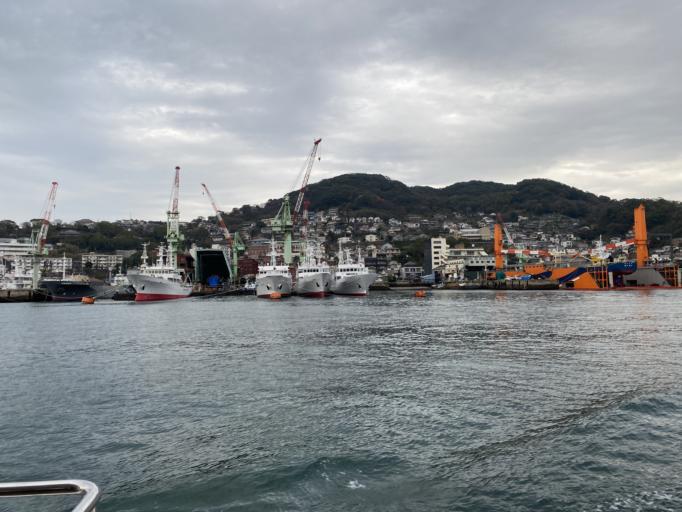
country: JP
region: Nagasaki
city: Nagasaki-shi
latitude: 32.7346
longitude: 129.8632
